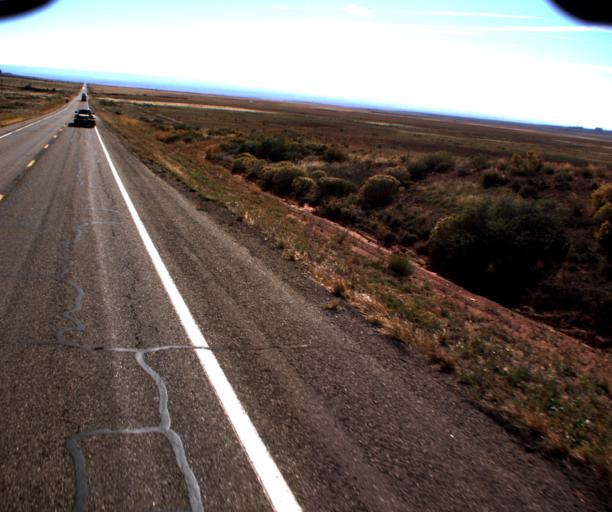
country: US
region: Arizona
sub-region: Mohave County
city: Colorado City
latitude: 36.8787
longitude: -112.8860
